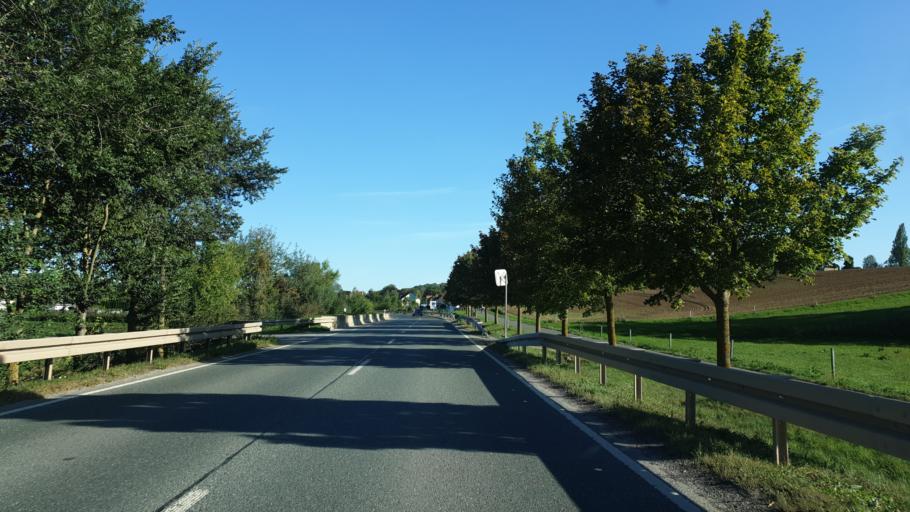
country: DE
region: Thuringia
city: Caaschwitz
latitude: 50.9379
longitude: 11.9989
